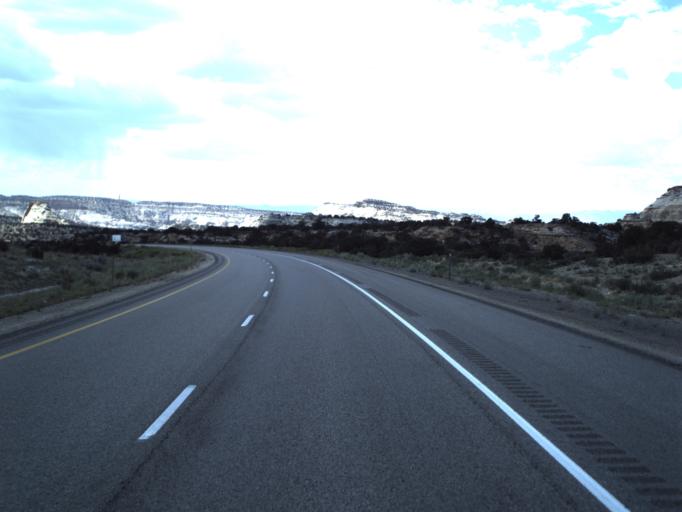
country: US
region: Utah
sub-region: Emery County
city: Ferron
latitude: 38.8648
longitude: -110.8479
